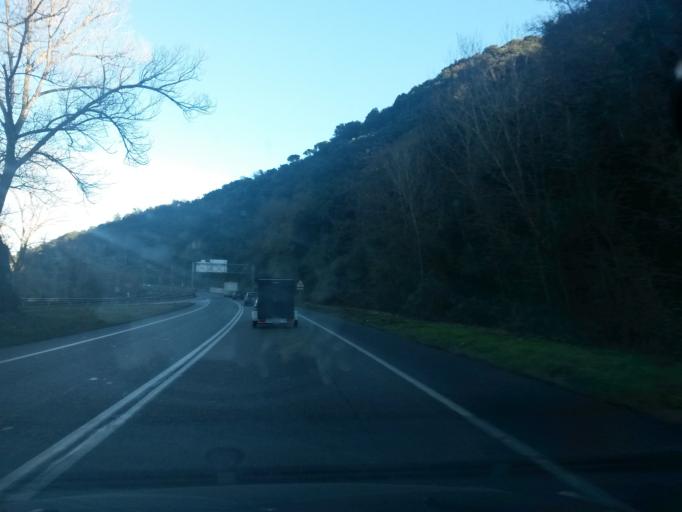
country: ES
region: Catalonia
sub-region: Provincia de Girona
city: Sant Julia de Ramis
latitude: 42.0218
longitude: 2.8528
